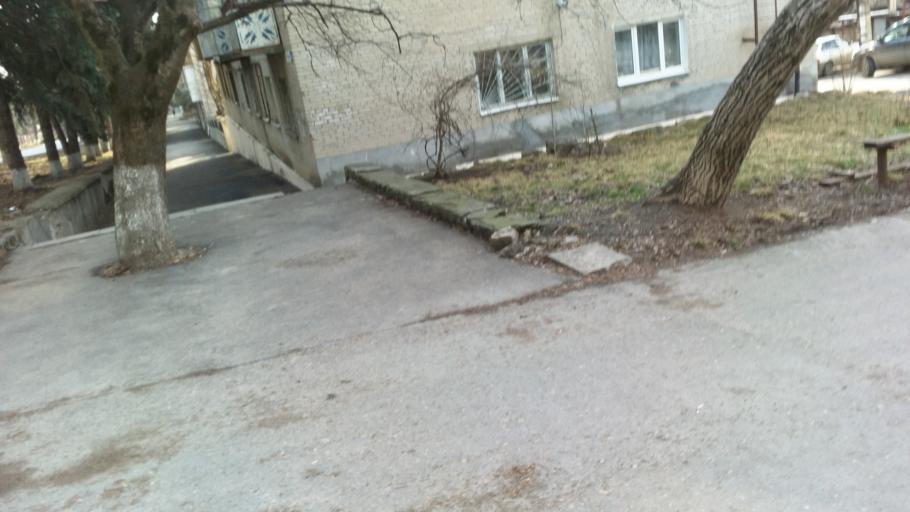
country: RU
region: Stavropol'skiy
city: Zheleznovodsk
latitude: 44.1327
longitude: 43.0430
